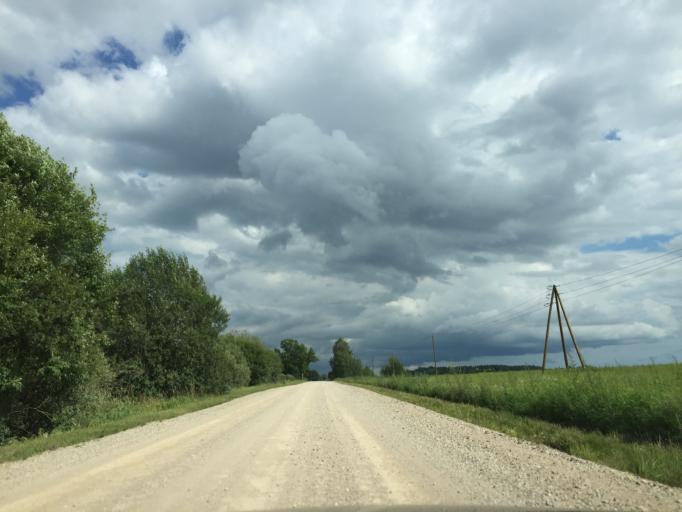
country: LV
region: Malpils
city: Malpils
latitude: 56.8557
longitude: 25.0377
